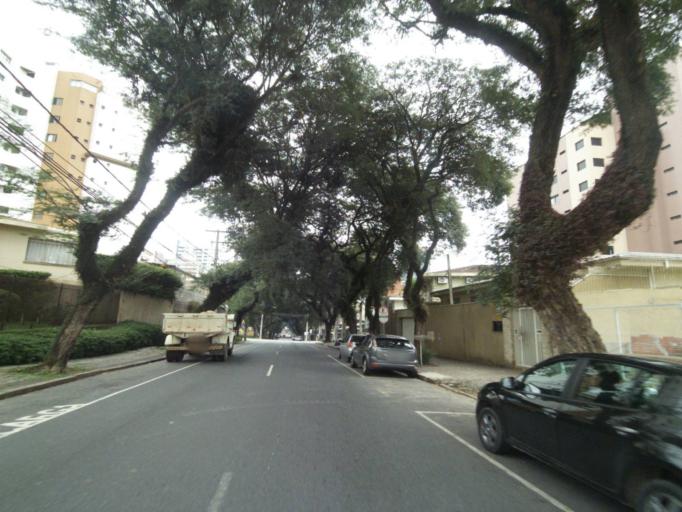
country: BR
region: Parana
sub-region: Curitiba
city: Curitiba
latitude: -25.4320
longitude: -49.2886
